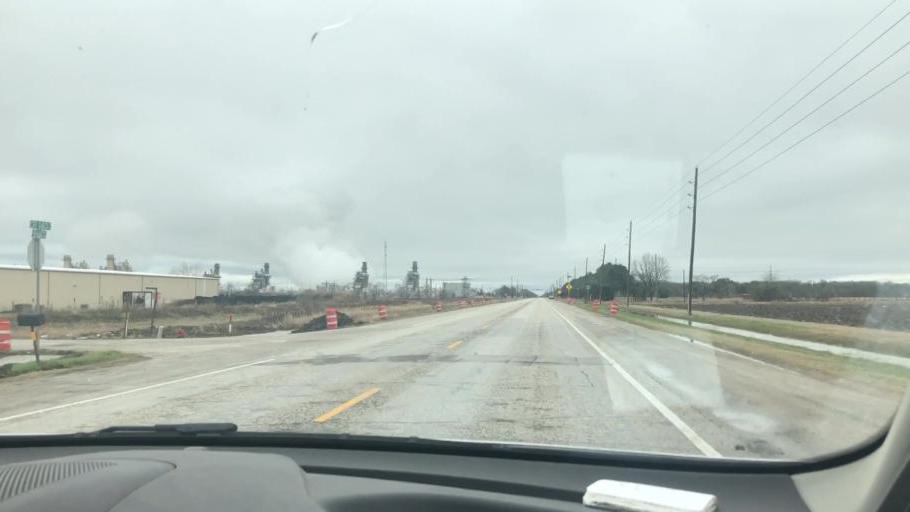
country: US
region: Texas
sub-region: Wharton County
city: Wharton
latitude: 29.2940
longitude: -96.0744
